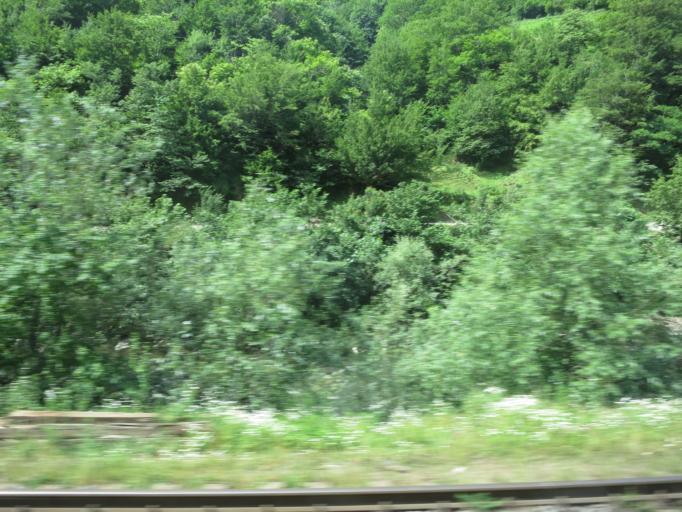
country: GE
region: Imereti
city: Kharagauli
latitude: 42.0071
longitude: 43.2150
